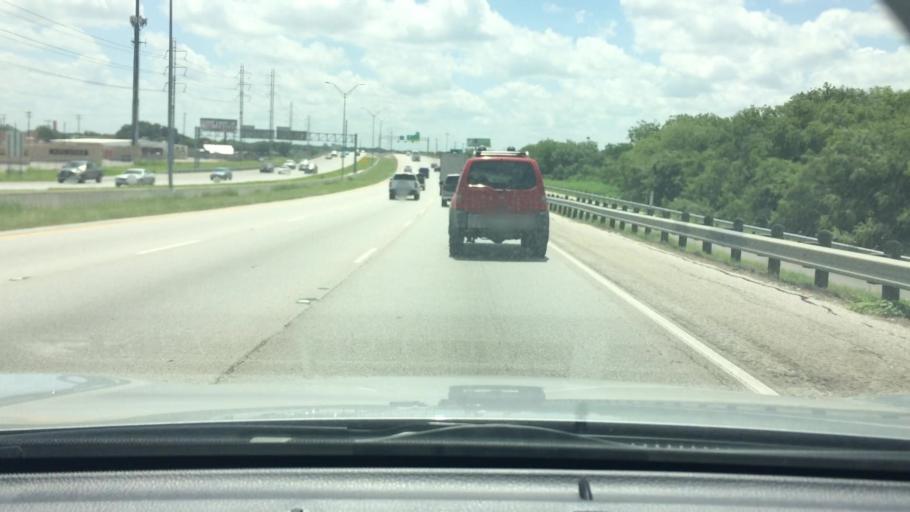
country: US
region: Texas
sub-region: Bexar County
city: San Antonio
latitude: 29.3616
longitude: -98.4413
